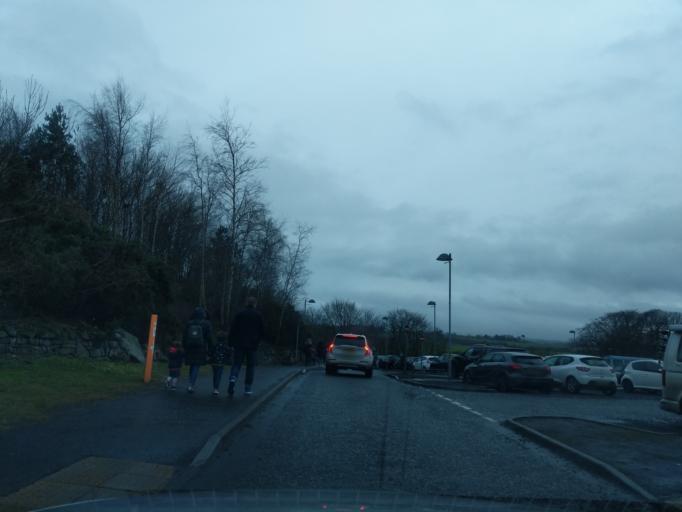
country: GB
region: Scotland
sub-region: Edinburgh
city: Newbridge
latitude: 55.9237
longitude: -3.3992
